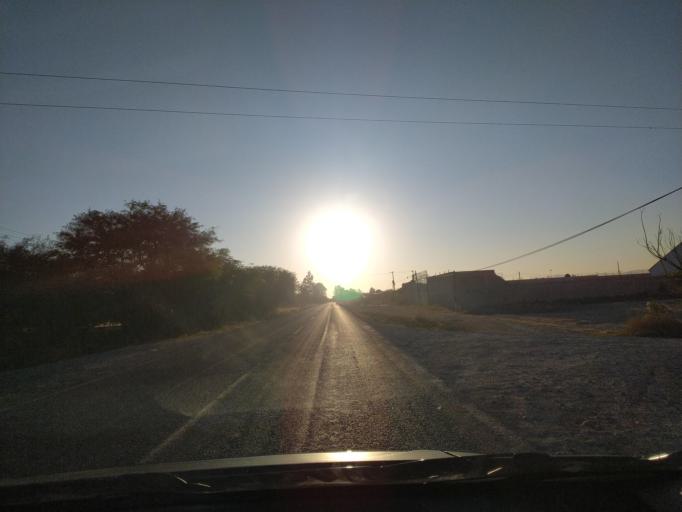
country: MX
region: Guanajuato
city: Ciudad Manuel Doblado
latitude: 20.7407
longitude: -101.9180
